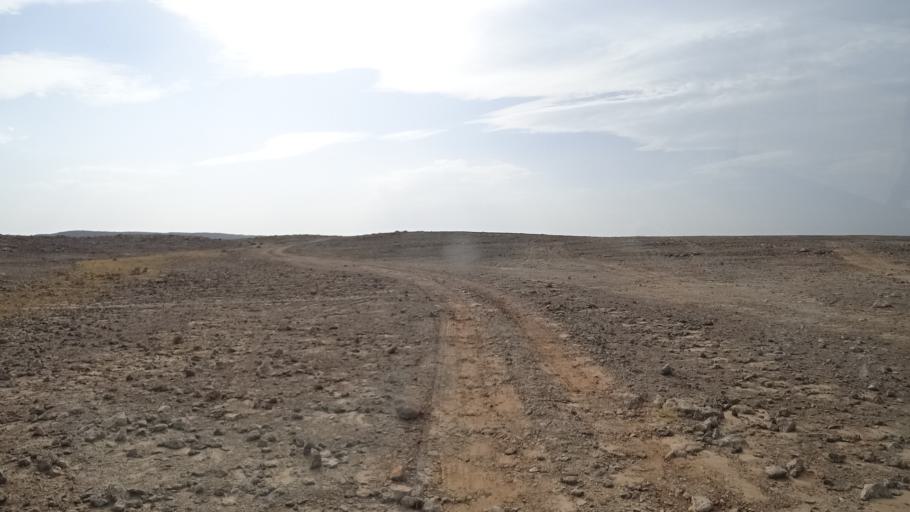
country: OM
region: Ash Sharqiyah
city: Sur
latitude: 22.4571
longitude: 59.8278
